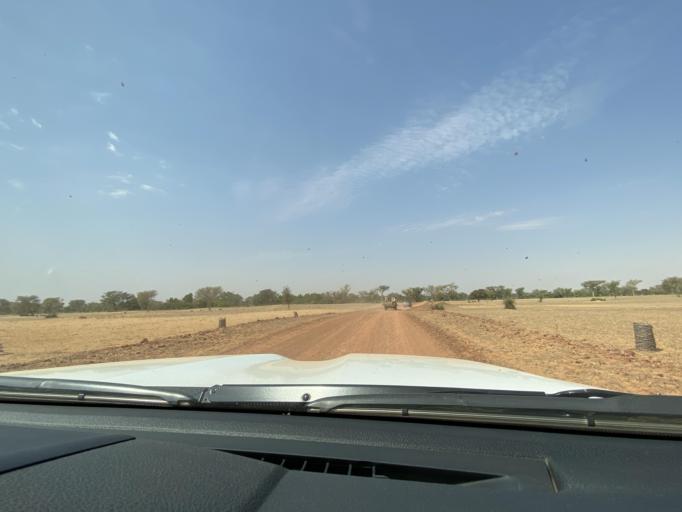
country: NE
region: Dosso
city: Birnin Gaoure
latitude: 13.2451
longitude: 2.8608
